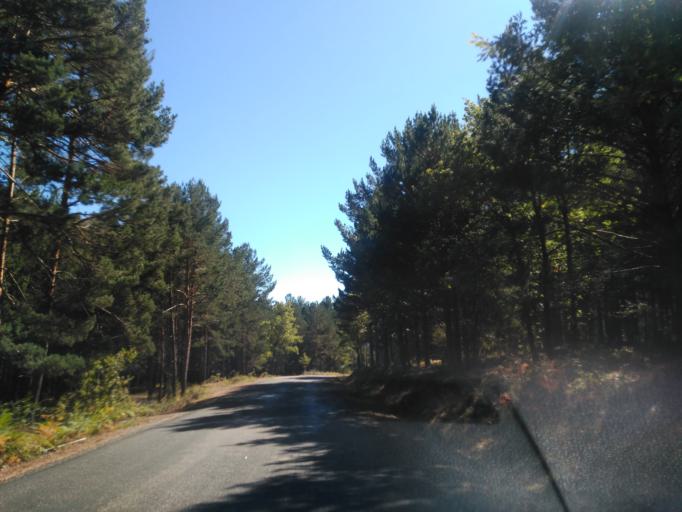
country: ES
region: Castille and Leon
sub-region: Provincia de Soria
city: Vinuesa
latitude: 41.9660
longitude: -2.7899
